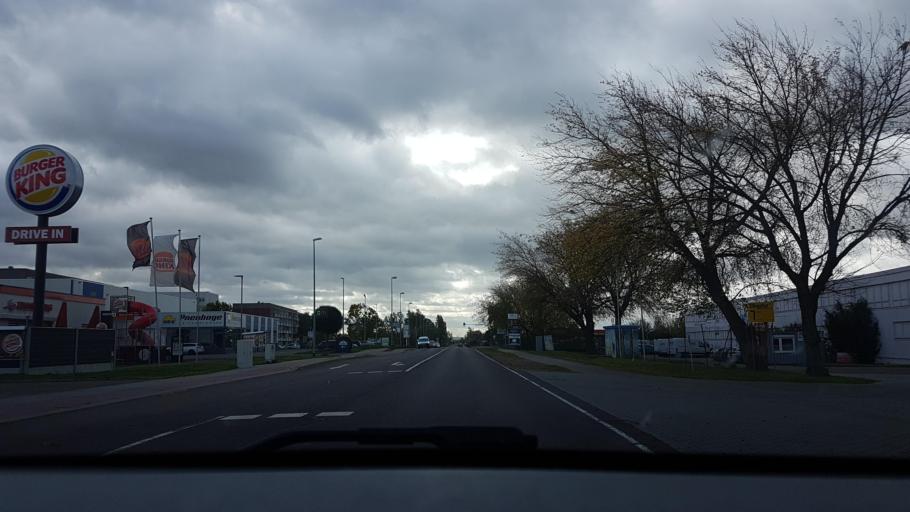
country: DE
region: Saxony-Anhalt
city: Bernburg
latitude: 51.7791
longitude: 11.7468
